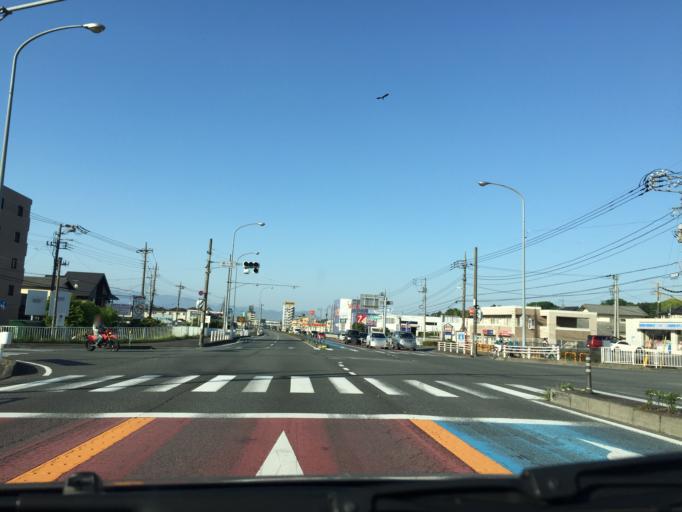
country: JP
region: Shizuoka
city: Mishima
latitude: 35.1585
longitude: 138.8988
